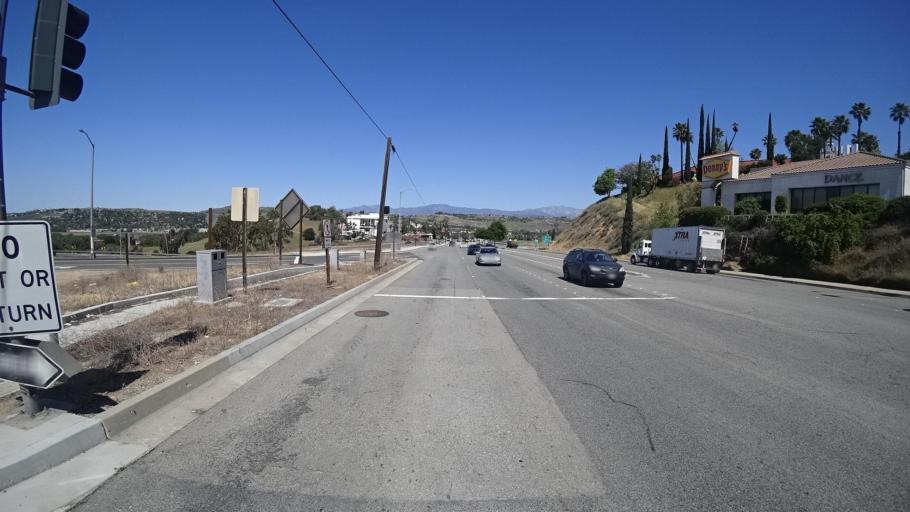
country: US
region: California
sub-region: Los Angeles County
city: Diamond Bar
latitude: 34.0419
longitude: -117.7998
